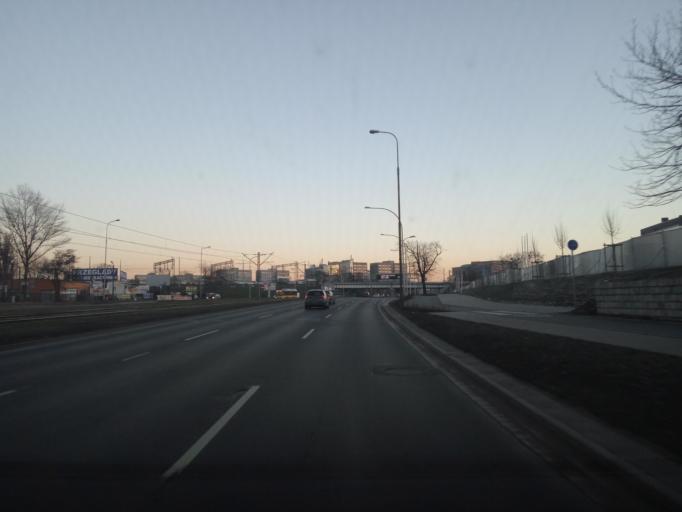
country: PL
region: Lower Silesian Voivodeship
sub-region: Powiat wroclawski
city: Wroclaw
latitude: 51.1199
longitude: 16.9962
